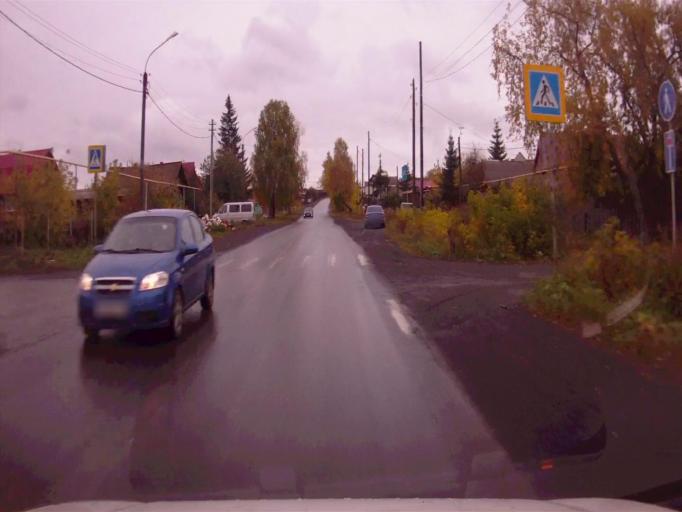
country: RU
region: Chelyabinsk
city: Verkhniy Ufaley
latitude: 56.0493
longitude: 60.2067
